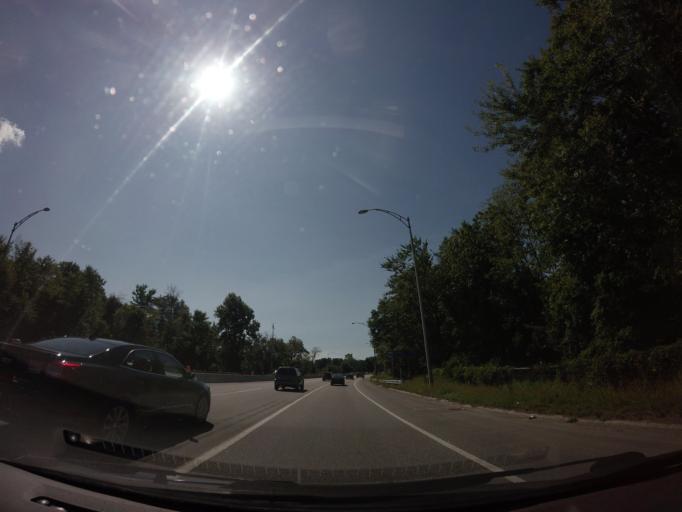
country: CA
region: Quebec
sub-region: Outaouais
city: Gatineau
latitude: 45.4517
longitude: -75.7161
